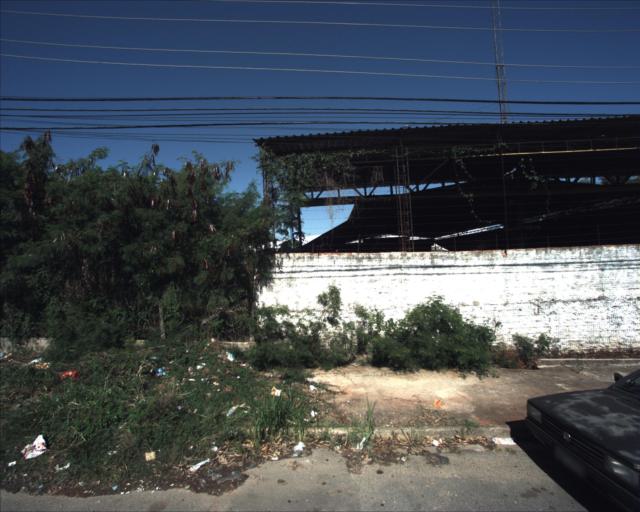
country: BR
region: Sao Paulo
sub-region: Sorocaba
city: Sorocaba
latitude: -23.4729
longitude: -47.4878
